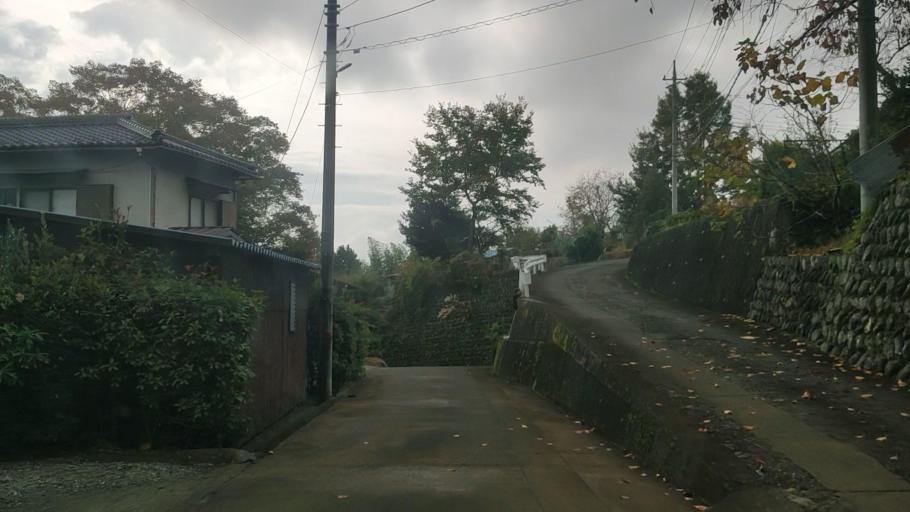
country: JP
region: Shizuoka
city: Fujinomiya
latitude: 35.3177
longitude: 138.4370
